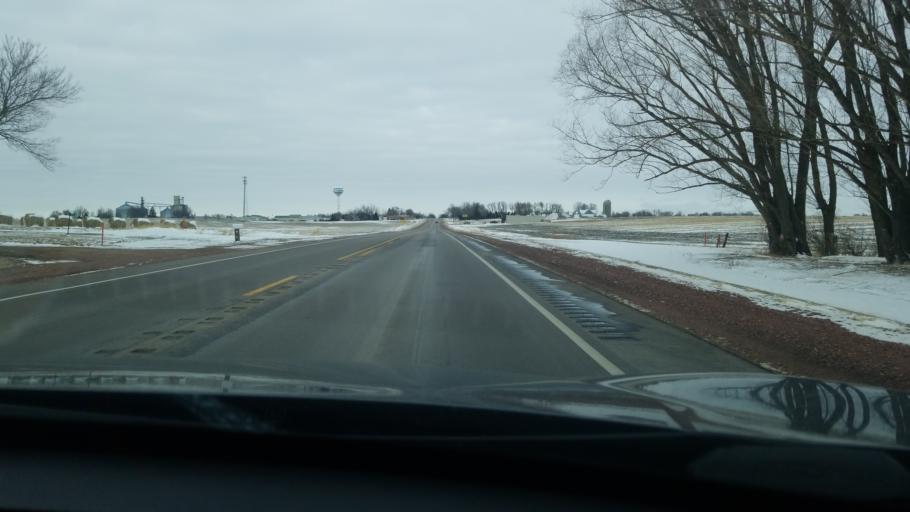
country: US
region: South Dakota
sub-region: Minnehaha County
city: Brandon
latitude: 43.4398
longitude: -96.4292
